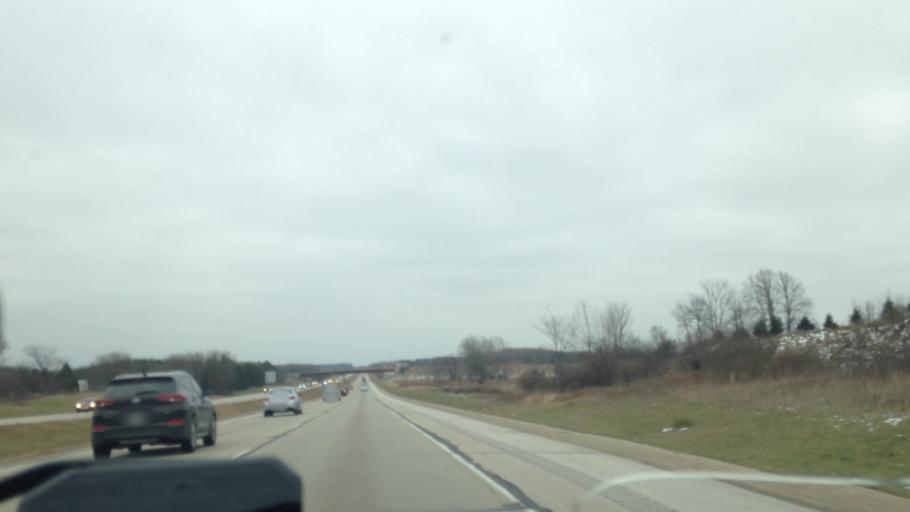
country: US
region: Wisconsin
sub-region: Washington County
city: Slinger
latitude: 43.3141
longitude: -88.2368
